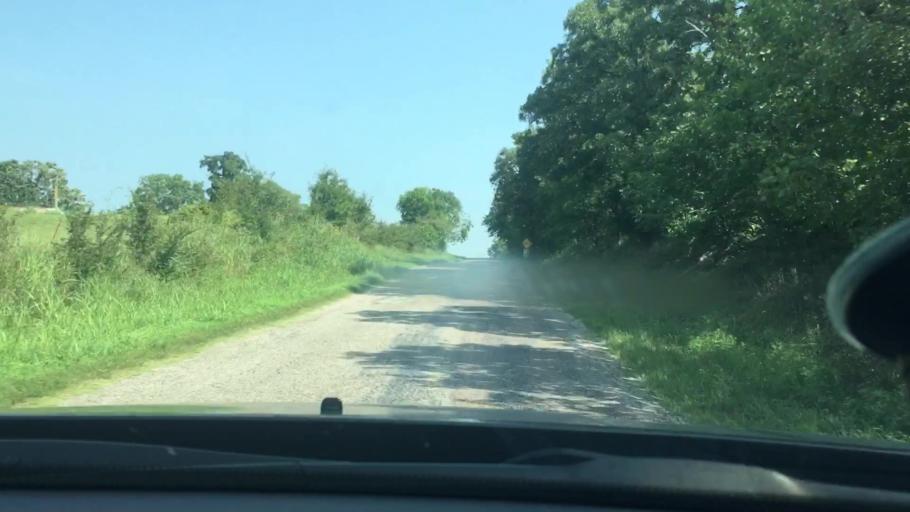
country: US
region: Oklahoma
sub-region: Pontotoc County
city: Ada
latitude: 34.6635
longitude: -96.5298
